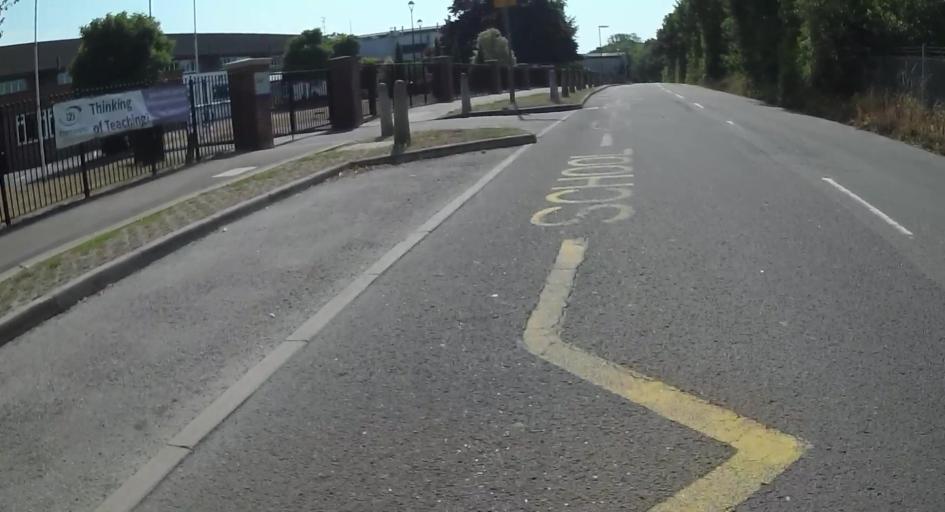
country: GB
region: England
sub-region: Surrey
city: Farnham
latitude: 51.2028
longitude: -0.8149
